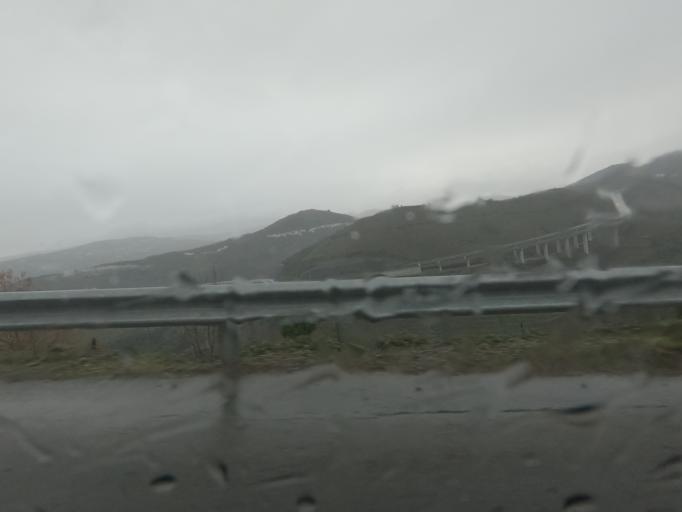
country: PT
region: Vila Real
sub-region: Peso da Regua
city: Peso da Regua
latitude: 41.1689
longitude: -7.7501
